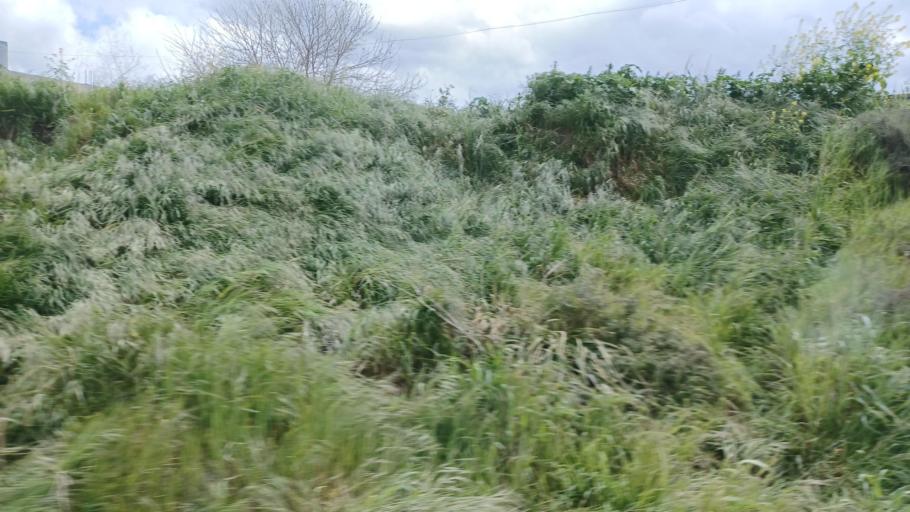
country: CY
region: Lefkosia
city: Lefka
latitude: 35.0778
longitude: 32.9260
